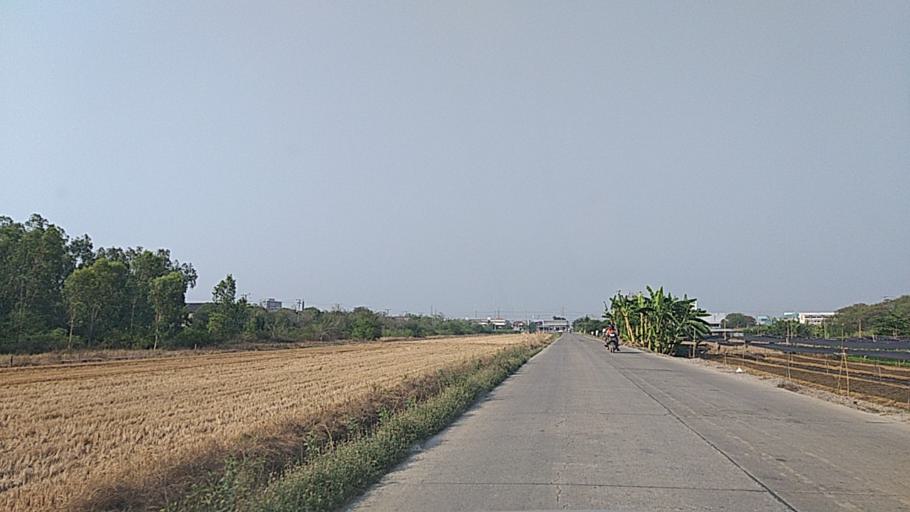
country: TH
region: Nonthaburi
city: Sai Noi
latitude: 13.9769
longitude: 100.3206
